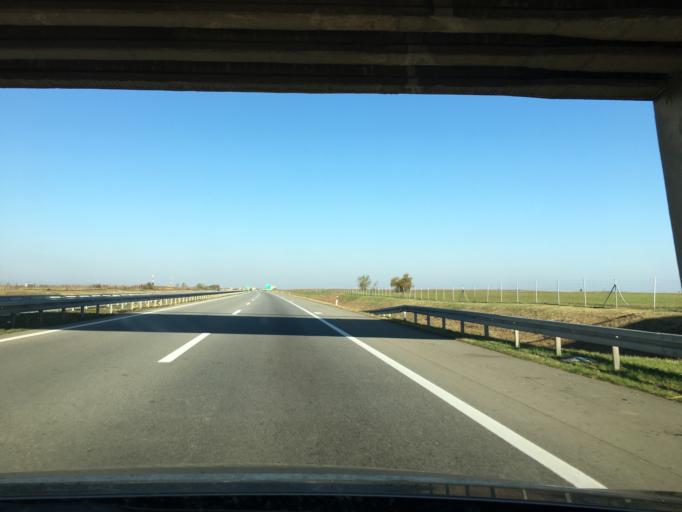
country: RS
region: Autonomna Pokrajina Vojvodina
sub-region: Juznobacki Okrug
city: Kovilj
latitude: 45.2288
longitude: 20.0529
